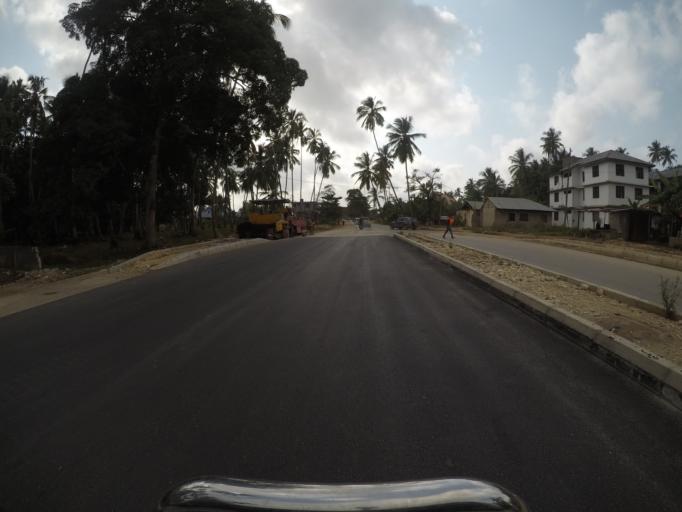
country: TZ
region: Zanzibar Central/South
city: Koani
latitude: -6.1959
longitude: 39.2771
